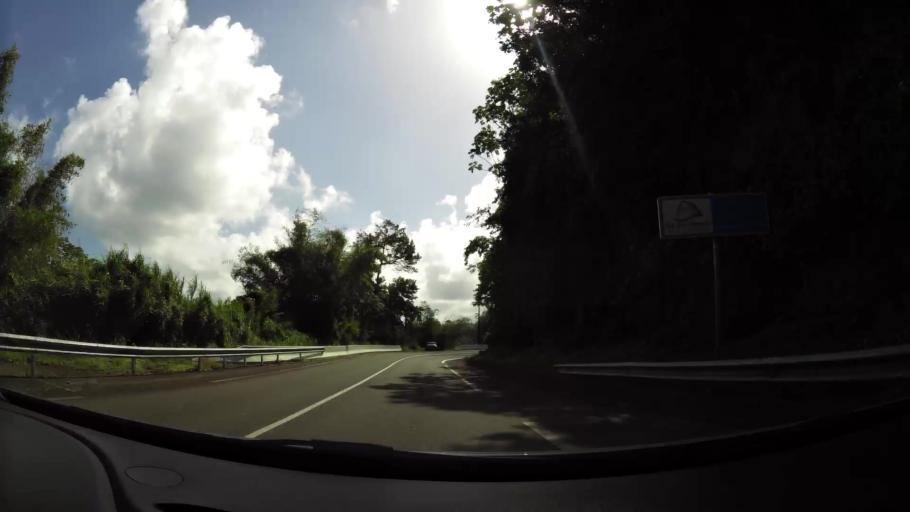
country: MQ
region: Martinique
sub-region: Martinique
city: Basse-Pointe
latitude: 14.8322
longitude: -61.1012
